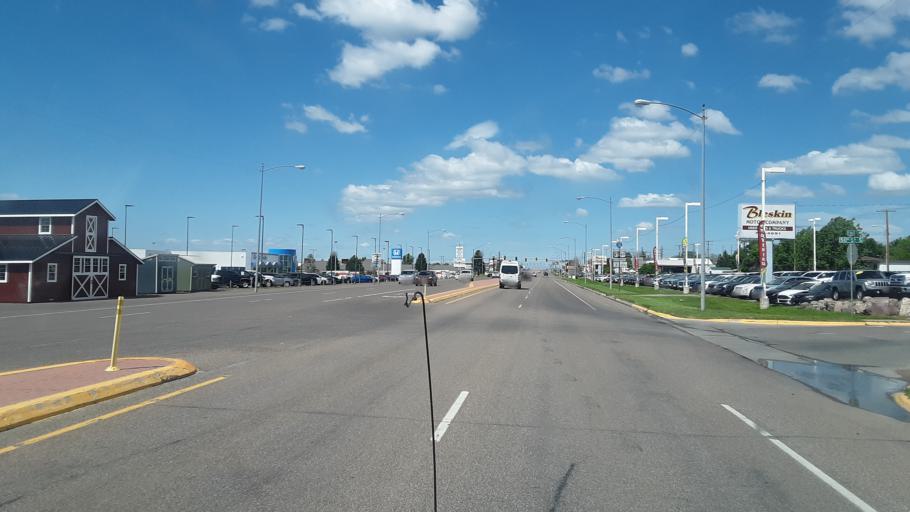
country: US
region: Montana
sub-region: Cascade County
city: Malmstrom Air Force Base
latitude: 47.4939
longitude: -111.2229
